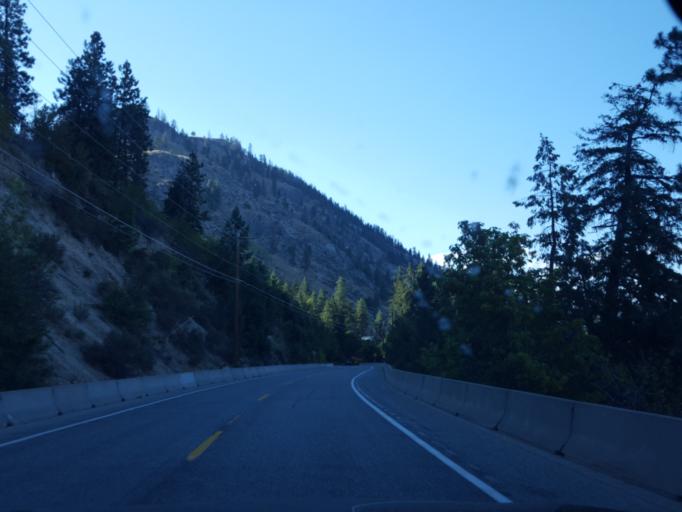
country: US
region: Washington
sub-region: Chelan County
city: Granite Falls
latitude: 47.8873
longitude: -120.2133
